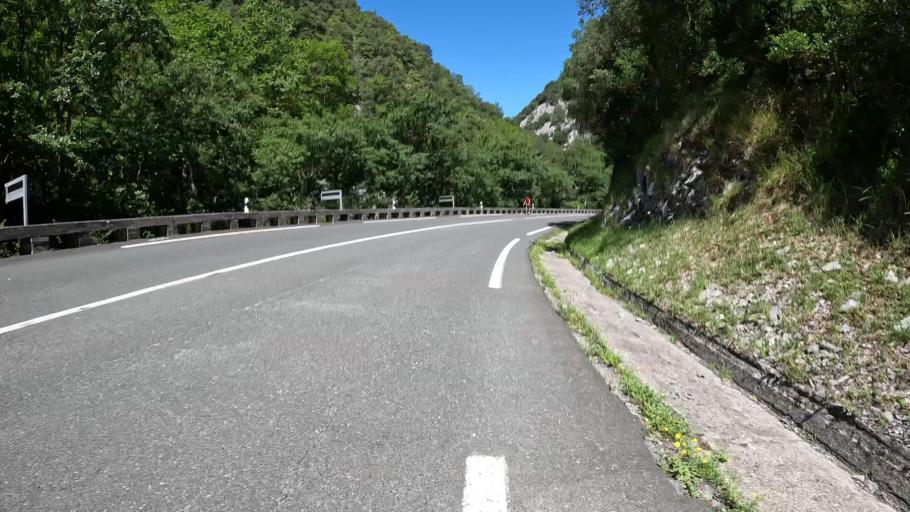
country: ES
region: Basque Country
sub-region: Provincia de Guipuzcoa
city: Oreja
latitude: 43.0795
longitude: -2.0188
